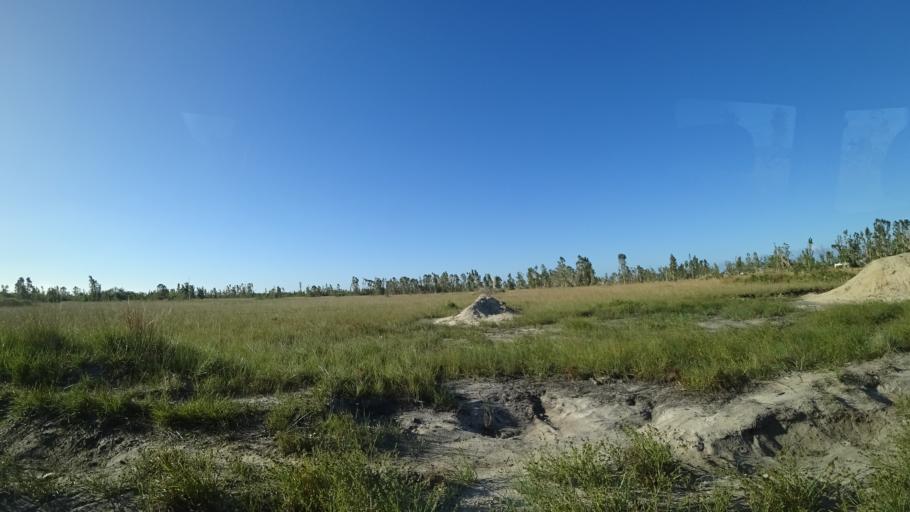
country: MZ
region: Sofala
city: Beira
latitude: -19.5758
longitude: 35.2544
